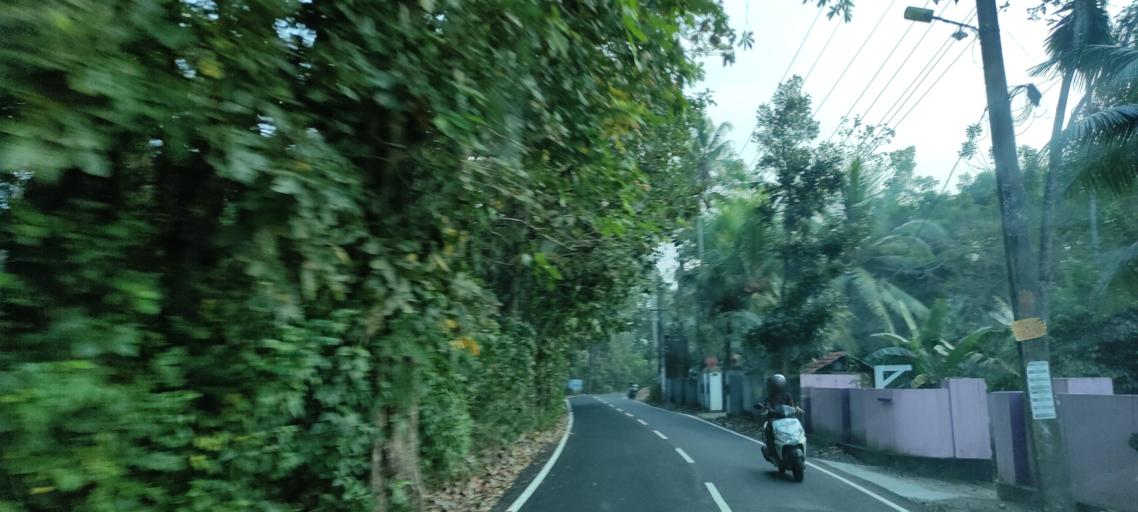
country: IN
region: Kerala
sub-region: Alappuzha
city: Mavelikara
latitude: 9.2717
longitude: 76.5522
